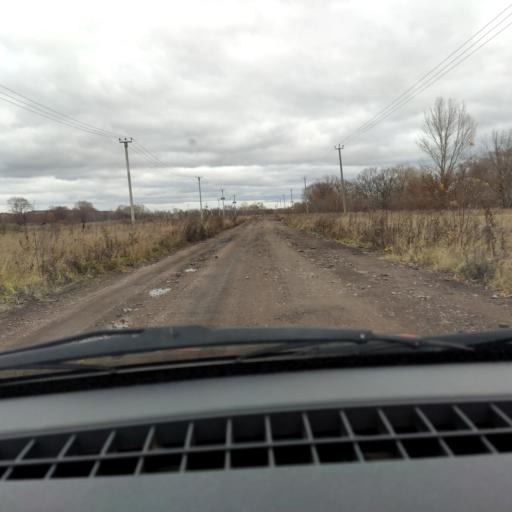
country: RU
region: Bashkortostan
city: Avdon
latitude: 54.4988
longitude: 55.8711
